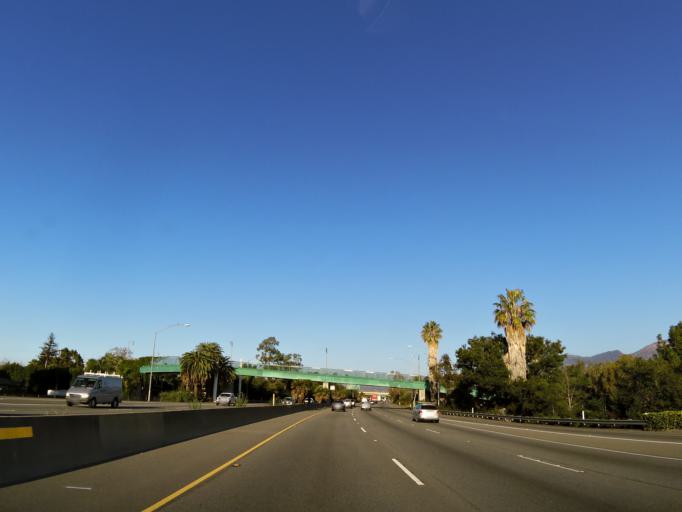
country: US
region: California
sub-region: Santa Barbara County
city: Santa Barbara
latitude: 34.4174
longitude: -119.7089
